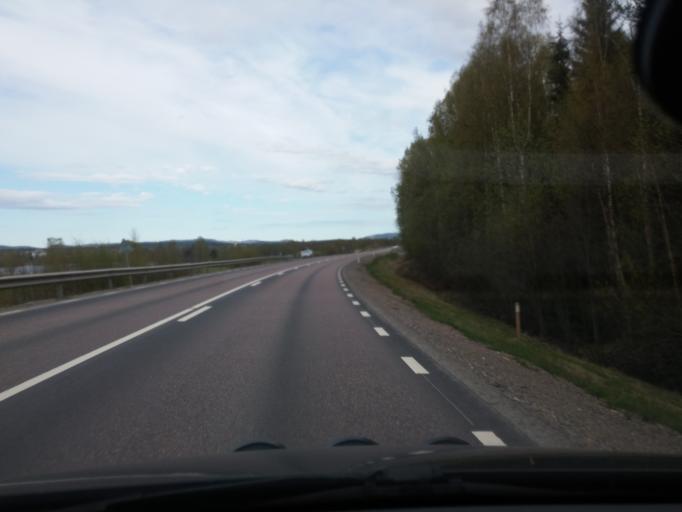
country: SE
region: Gaevleborg
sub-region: Ljusdals Kommun
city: Ljusdal
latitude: 61.8252
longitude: 16.0402
